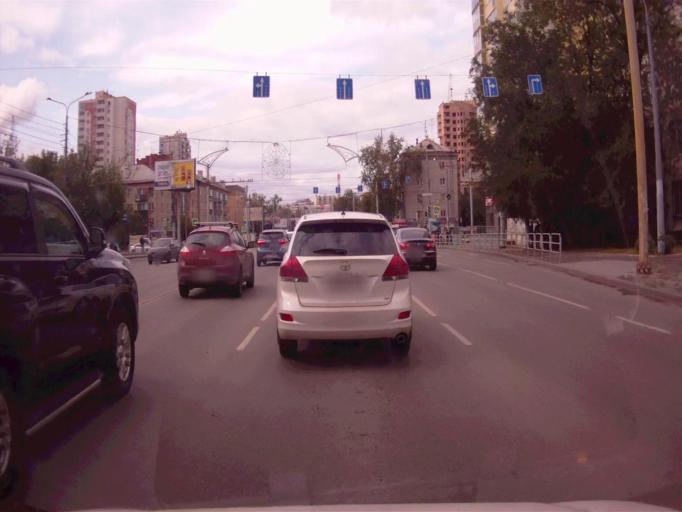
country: RU
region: Chelyabinsk
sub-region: Gorod Chelyabinsk
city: Chelyabinsk
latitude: 55.1441
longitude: 61.3877
